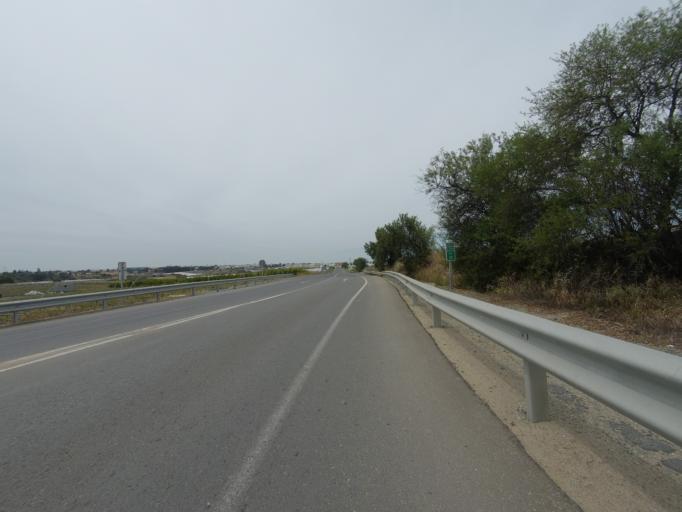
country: ES
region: Andalusia
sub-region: Provincia de Huelva
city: Palos de la Frontera
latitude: 37.2401
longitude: -6.8822
